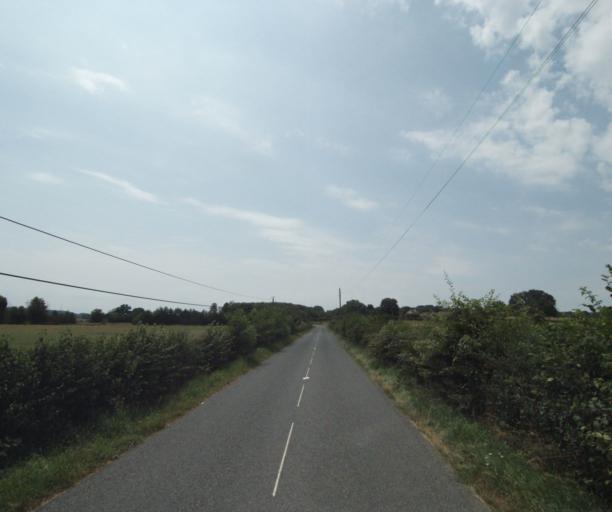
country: FR
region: Bourgogne
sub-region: Departement de Saone-et-Loire
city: Gueugnon
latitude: 46.5858
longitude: 4.0500
